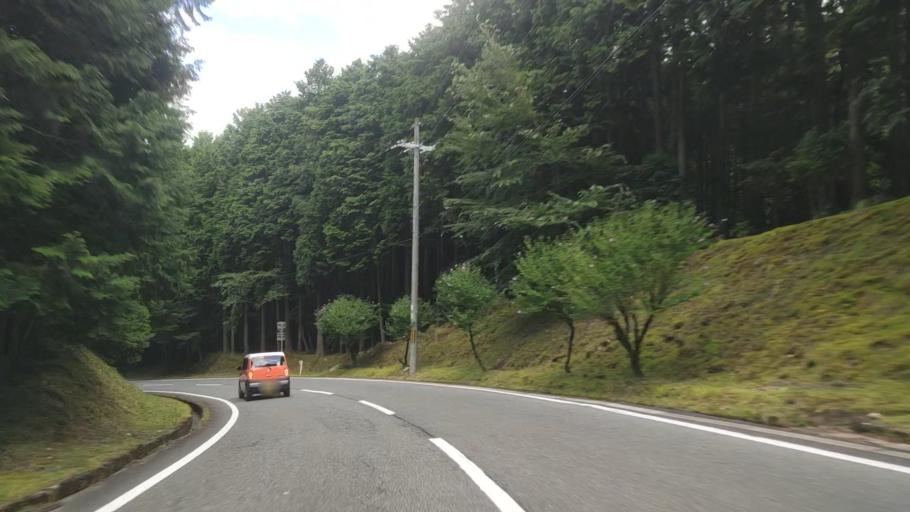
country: JP
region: Hyogo
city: Toyooka
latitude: 35.5384
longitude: 134.9779
